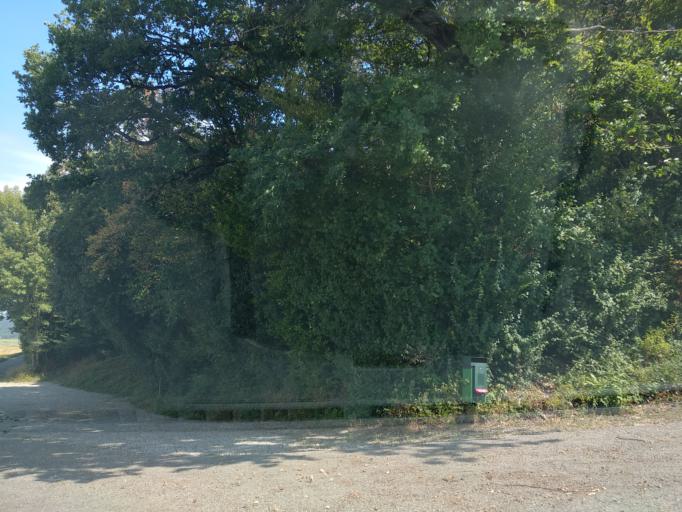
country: CH
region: Thurgau
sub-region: Frauenfeld District
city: Huttwilen
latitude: 47.5996
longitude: 8.8188
